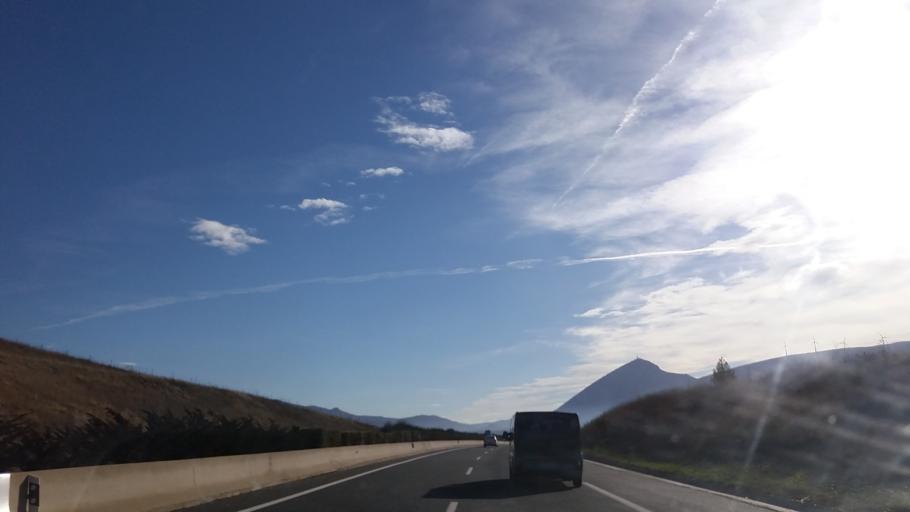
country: ES
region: Navarre
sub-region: Provincia de Navarra
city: Beriain
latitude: 42.7522
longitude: -1.6102
